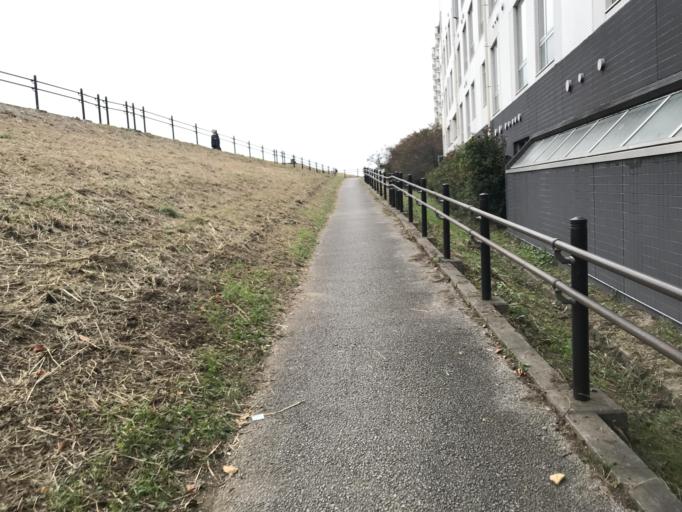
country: JP
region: Kanagawa
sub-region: Kawasaki-shi
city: Kawasaki
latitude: 35.5736
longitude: 139.6759
